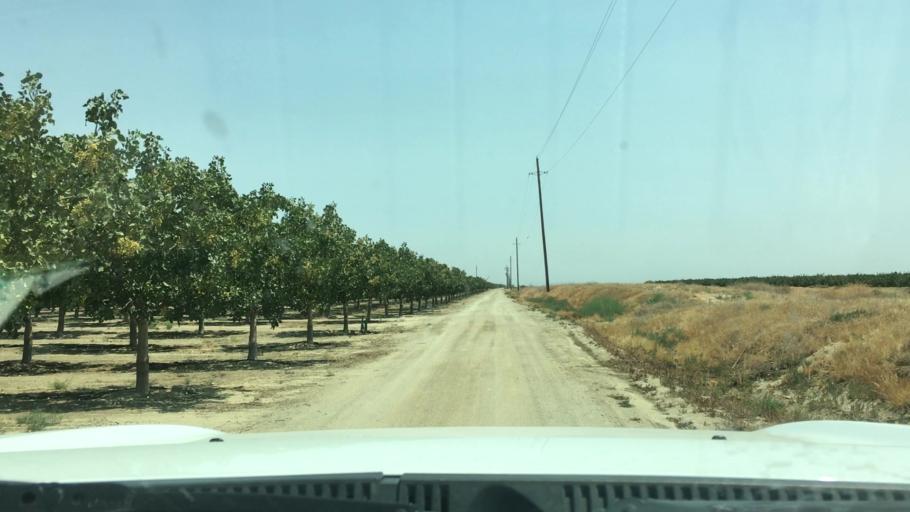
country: US
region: California
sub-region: Kern County
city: Wasco
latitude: 35.6814
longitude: -119.4245
